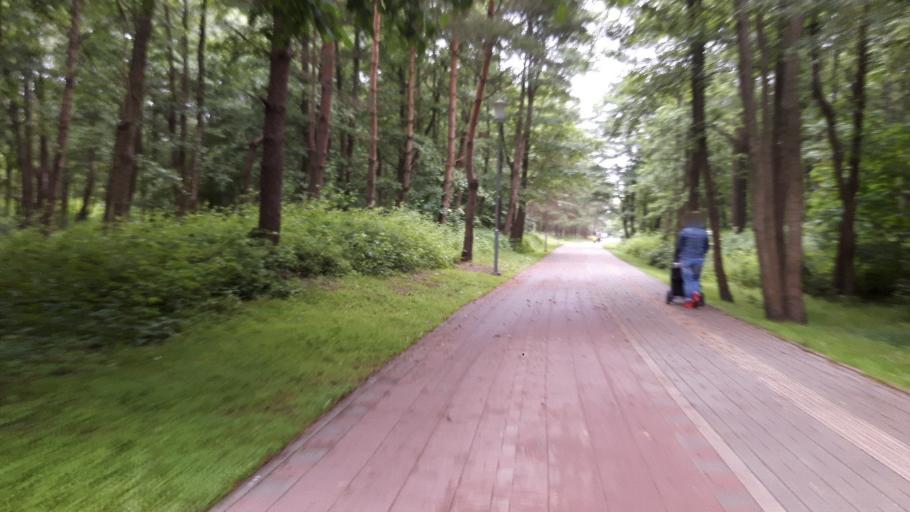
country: LV
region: Liepaja
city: Liepaja
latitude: 56.4895
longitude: 20.9986
